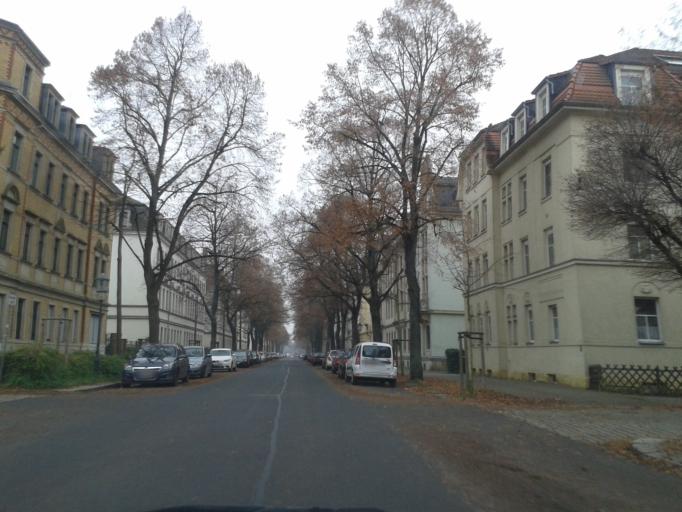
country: DE
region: Saxony
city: Albertstadt
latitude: 51.0937
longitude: 13.7261
